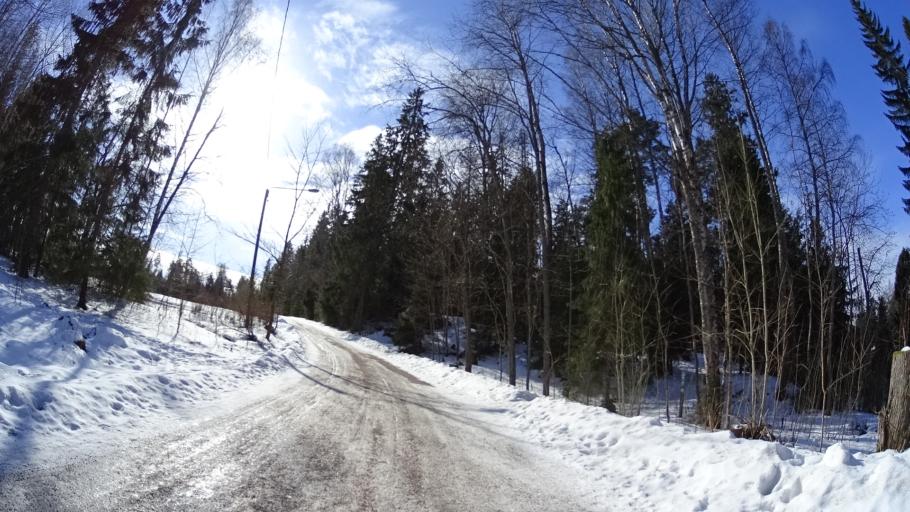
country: FI
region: Uusimaa
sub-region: Helsinki
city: Kauniainen
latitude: 60.2269
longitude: 24.6928
